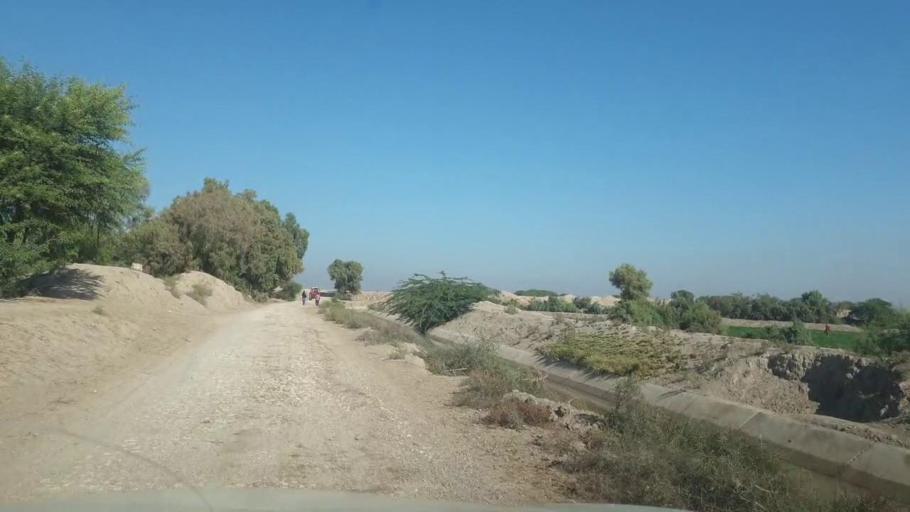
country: PK
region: Sindh
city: Bhan
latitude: 26.5606
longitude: 67.6299
